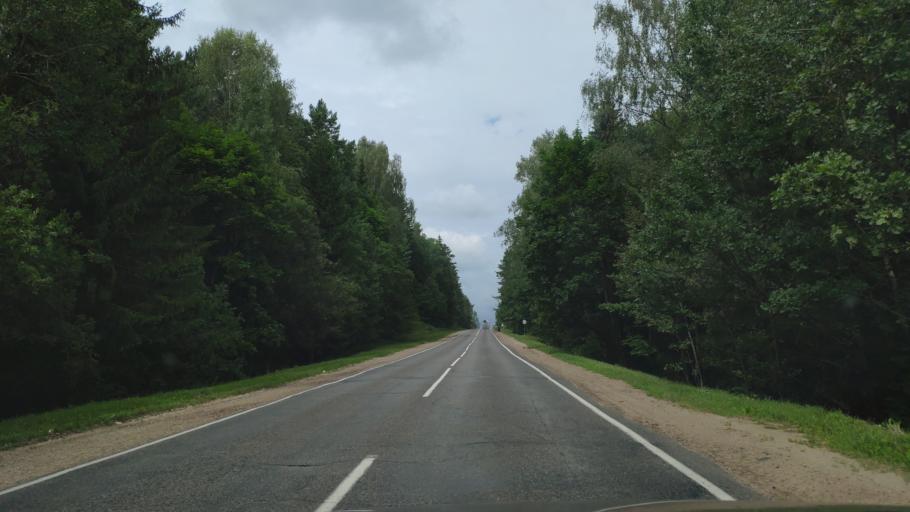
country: BY
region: Minsk
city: Novosel'ye
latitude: 53.9399
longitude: 27.2444
